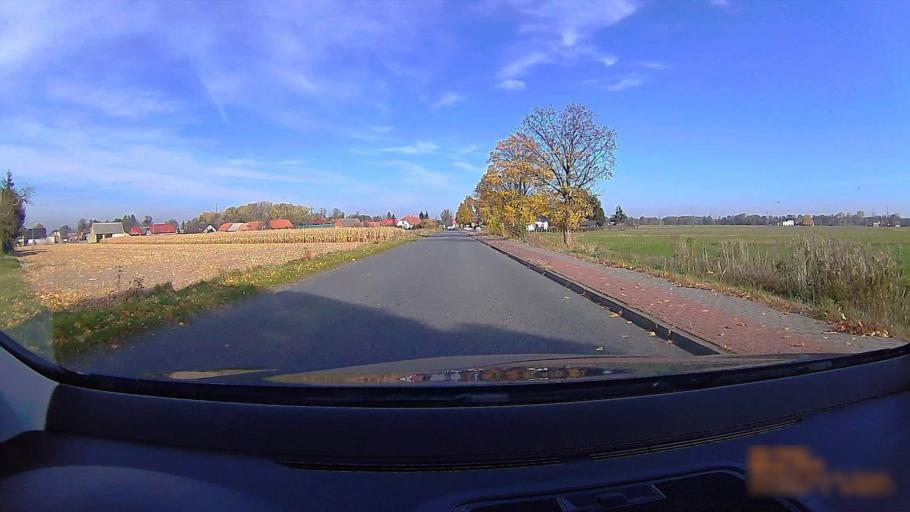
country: PL
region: Greater Poland Voivodeship
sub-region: Powiat ostrzeszowski
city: Doruchow
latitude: 51.4087
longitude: 18.0730
